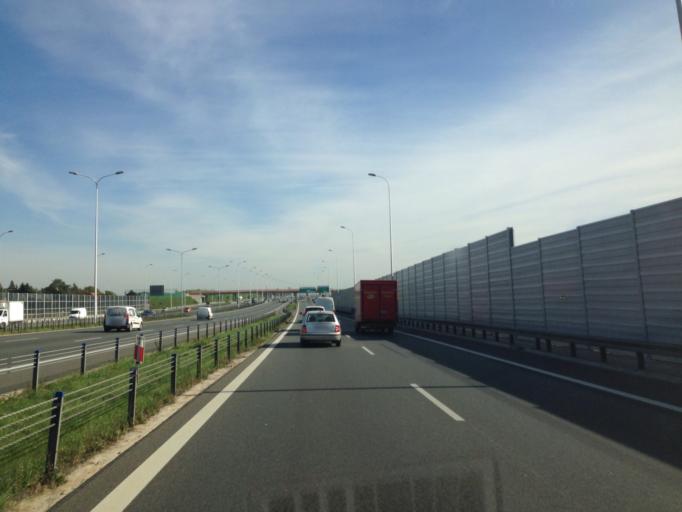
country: PL
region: Masovian Voivodeship
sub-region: Powiat pruszkowski
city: Michalowice
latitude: 52.1768
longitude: 20.8959
